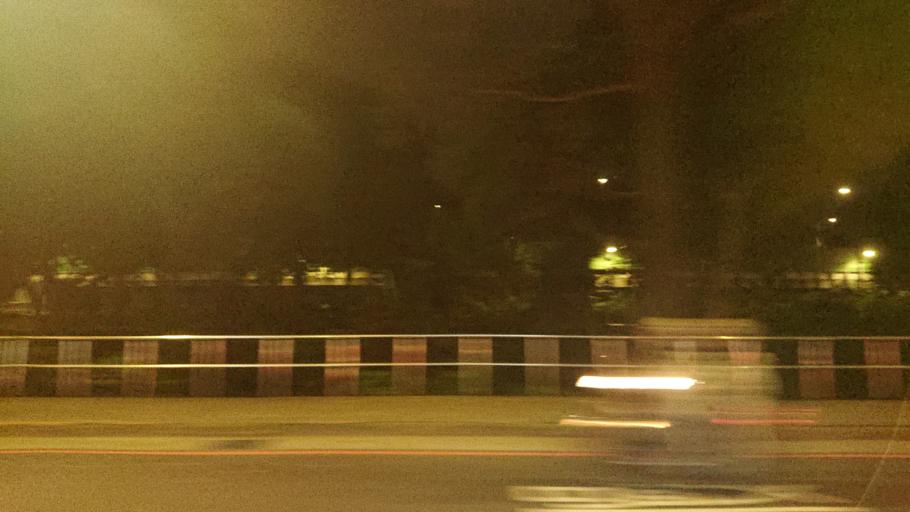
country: TW
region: Taipei
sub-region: Taipei
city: Banqiao
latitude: 24.9525
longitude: 121.4114
